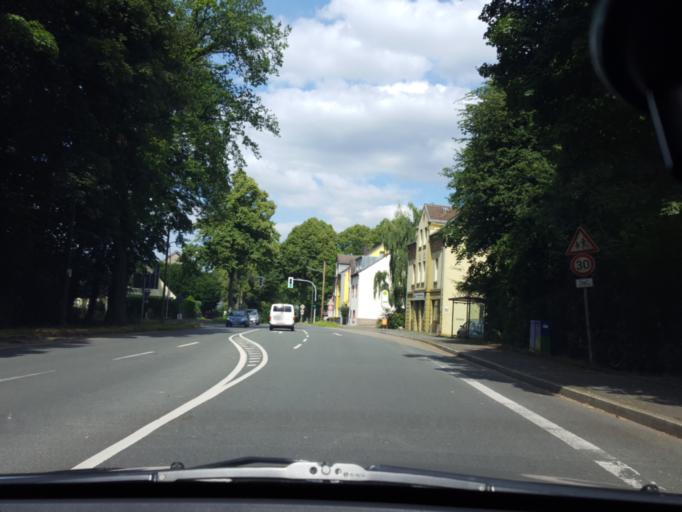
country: DE
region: North Rhine-Westphalia
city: Witten
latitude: 51.4594
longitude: 7.3359
